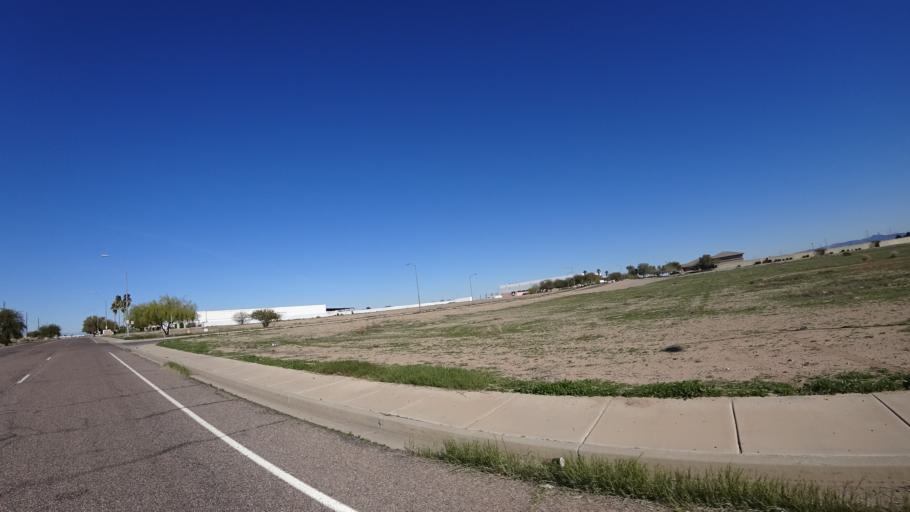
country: US
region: Arizona
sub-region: Maricopa County
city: Goodyear
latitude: 33.4095
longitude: -112.3751
